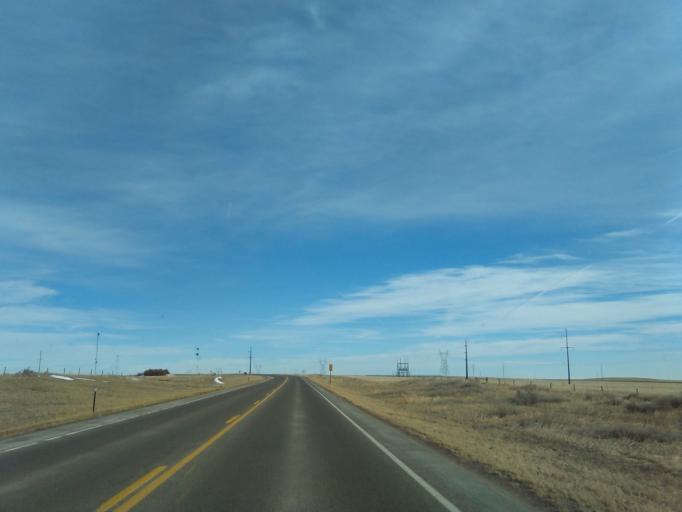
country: US
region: Wyoming
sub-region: Laramie County
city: Pine Bluffs
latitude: 41.4369
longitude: -104.3555
